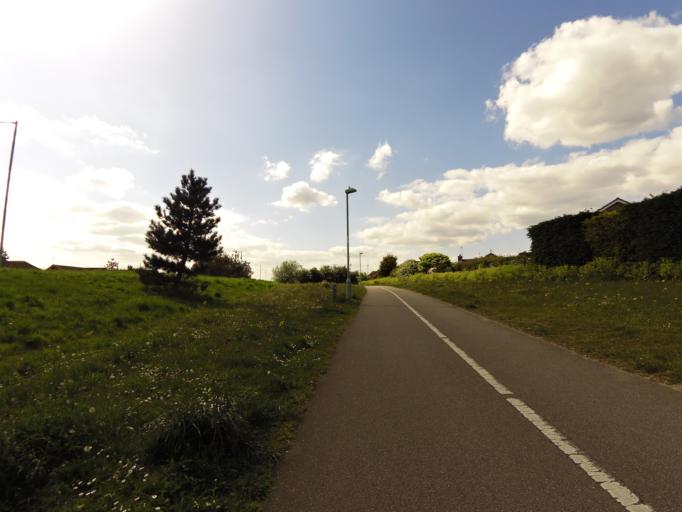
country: GB
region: England
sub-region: Suffolk
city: Kessingland
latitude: 52.4549
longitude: 1.7008
